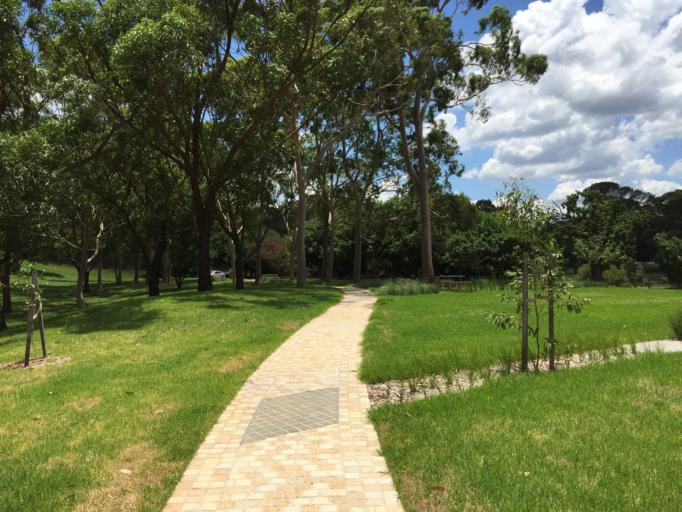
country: AU
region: New South Wales
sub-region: Parramatta
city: City of Parramatta
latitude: -33.8107
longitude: 150.9959
